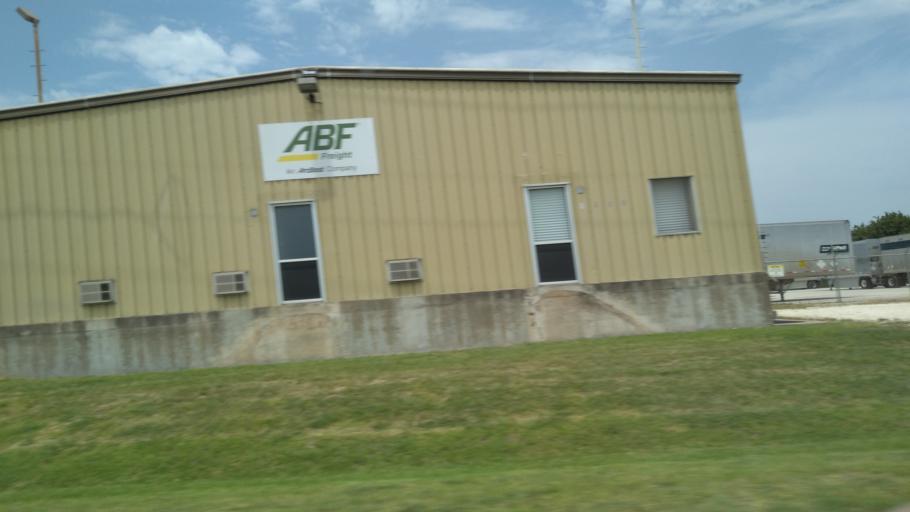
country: US
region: Texas
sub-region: McLennan County
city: Beverly Hills
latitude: 31.4815
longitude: -97.1586
